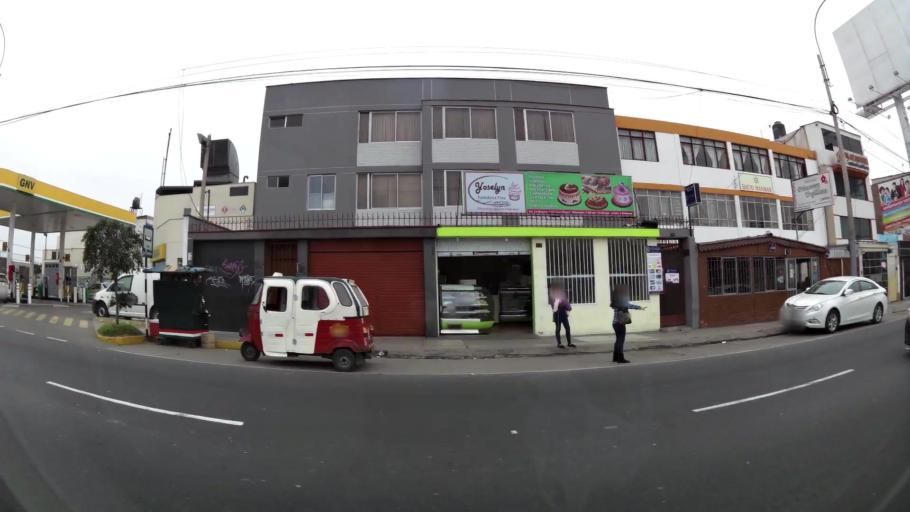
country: PE
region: Lima
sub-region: Lima
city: San Isidro
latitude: -12.0800
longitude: -77.0762
